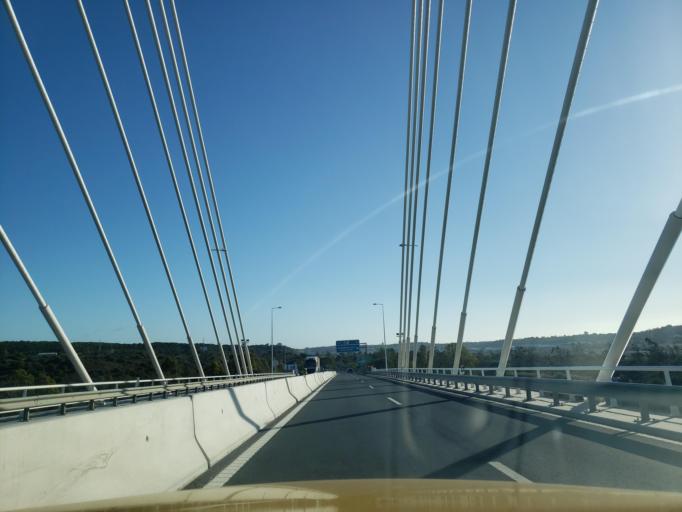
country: PT
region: Faro
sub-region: Castro Marim
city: Castro Marim
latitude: 37.2375
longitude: -7.4176
